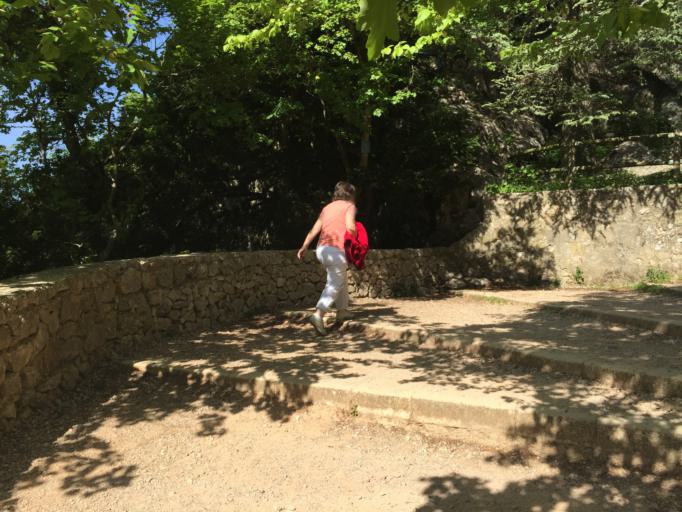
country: FR
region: Provence-Alpes-Cote d'Azur
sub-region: Departement du Var
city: Nans-les-Pins
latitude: 43.3274
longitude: 5.7646
